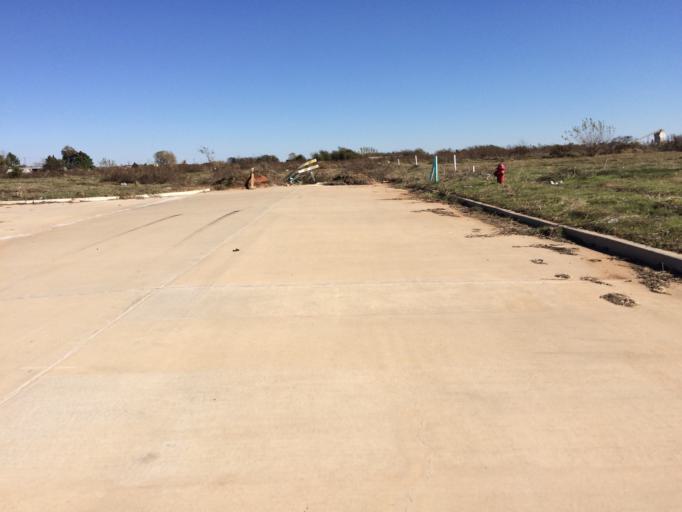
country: US
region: Oklahoma
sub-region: Cleveland County
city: Noble
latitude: 35.1717
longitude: -97.4182
